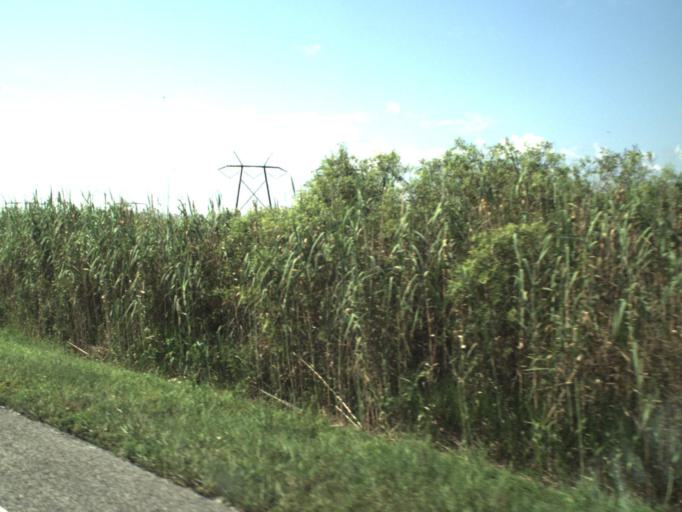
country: US
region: Florida
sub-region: Broward County
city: Weston
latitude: 26.2904
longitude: -80.5037
